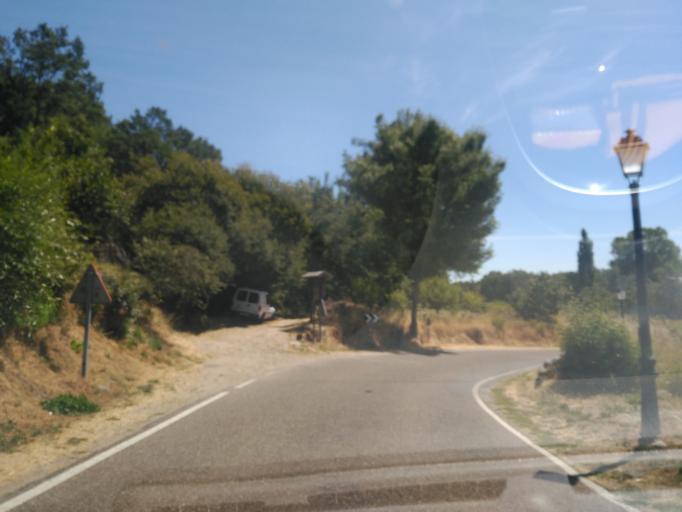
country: ES
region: Castille and Leon
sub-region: Provincia de Zamora
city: Galende
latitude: 42.1374
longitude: -6.7166
